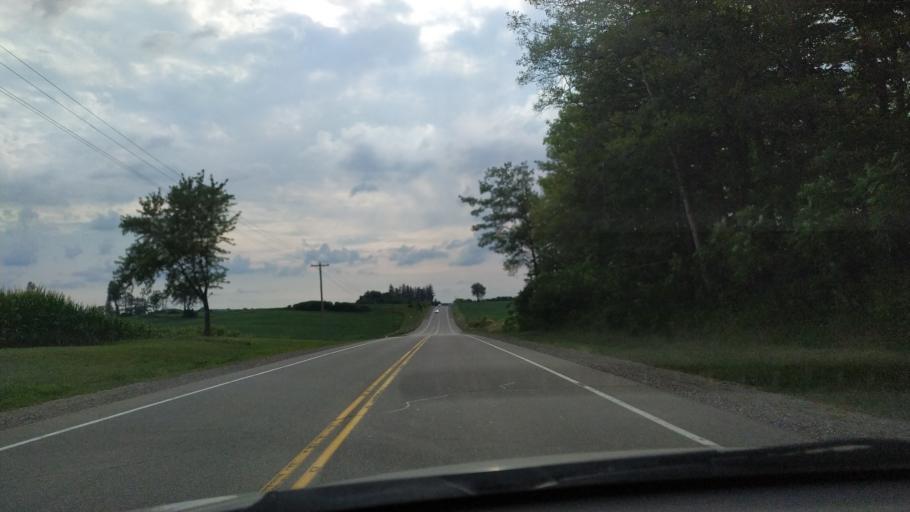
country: CA
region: Ontario
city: Kitchener
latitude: 43.3557
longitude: -80.4947
